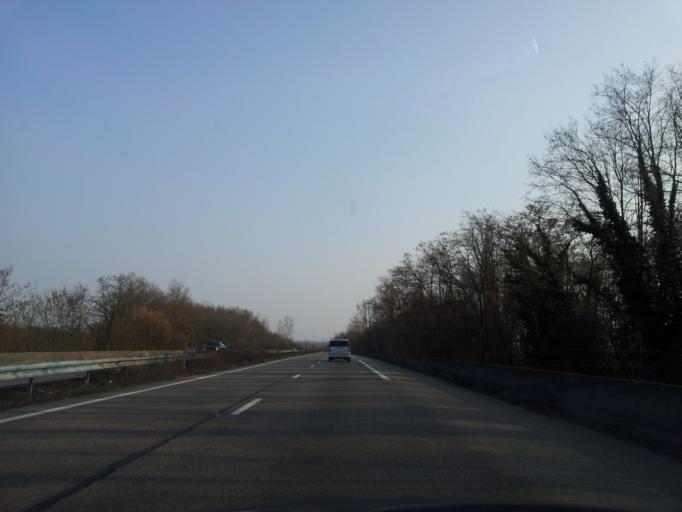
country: FR
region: Alsace
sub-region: Departement du Haut-Rhin
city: Blotzheim
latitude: 47.6204
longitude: 7.5121
